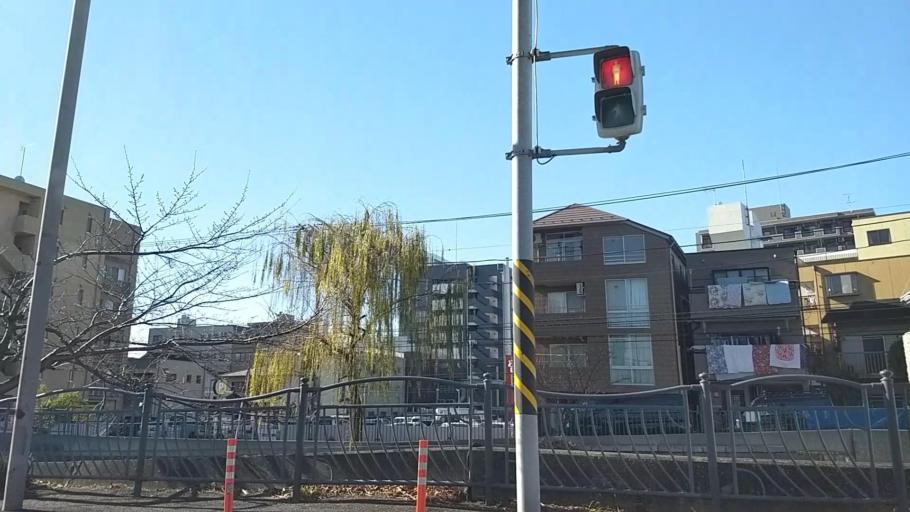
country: JP
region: Kanagawa
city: Yokohama
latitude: 35.4617
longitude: 139.6108
